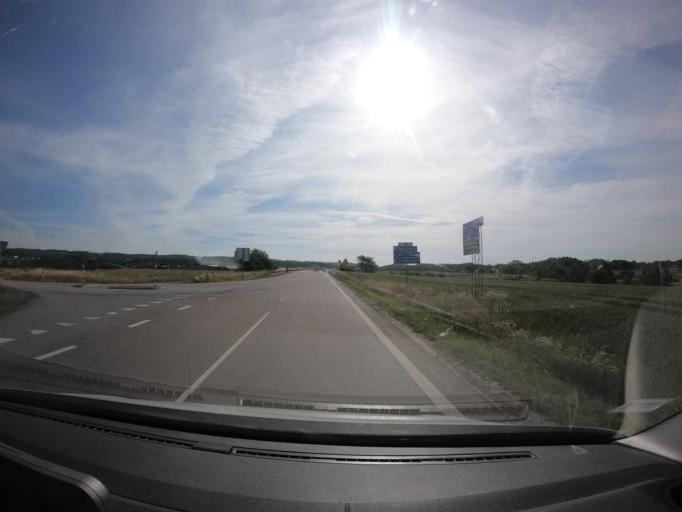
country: SE
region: Skane
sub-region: Bastads Kommun
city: Forslov
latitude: 56.3550
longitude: 12.7957
